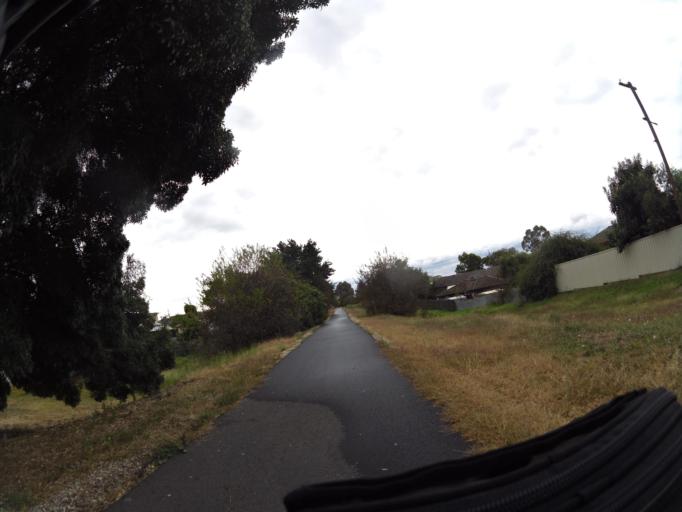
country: AU
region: Victoria
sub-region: Wodonga
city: Wodonga
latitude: -36.1267
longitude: 146.8947
